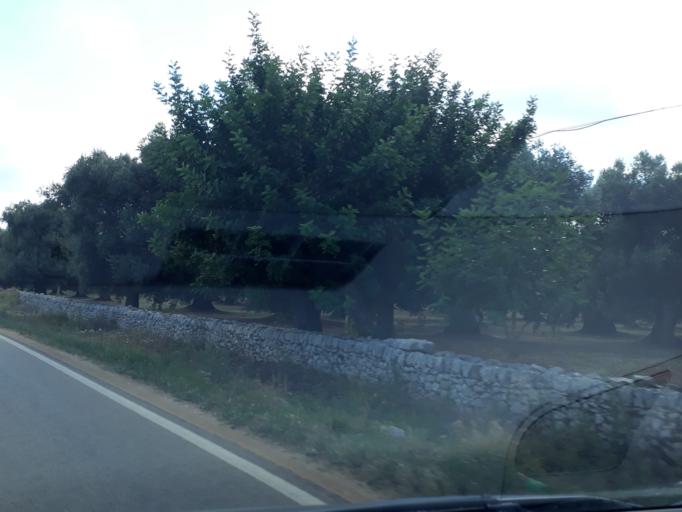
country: IT
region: Apulia
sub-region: Provincia di Brindisi
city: Pezze di Greco
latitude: 40.8130
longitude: 17.3822
